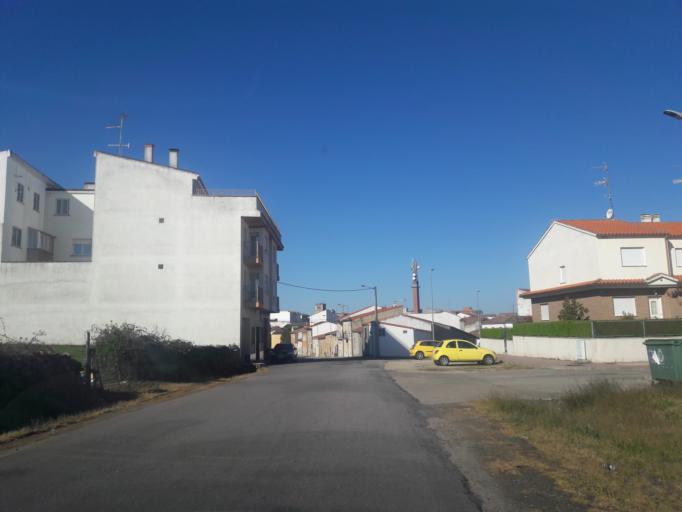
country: ES
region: Castille and Leon
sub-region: Provincia de Salamanca
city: Vitigudino
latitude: 41.0107
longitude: -6.4293
